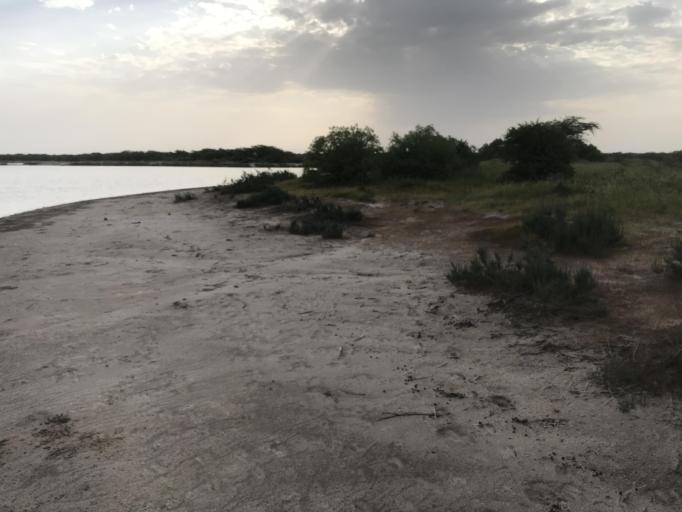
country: SN
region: Saint-Louis
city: Saint-Louis
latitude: 15.9302
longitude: -16.4624
